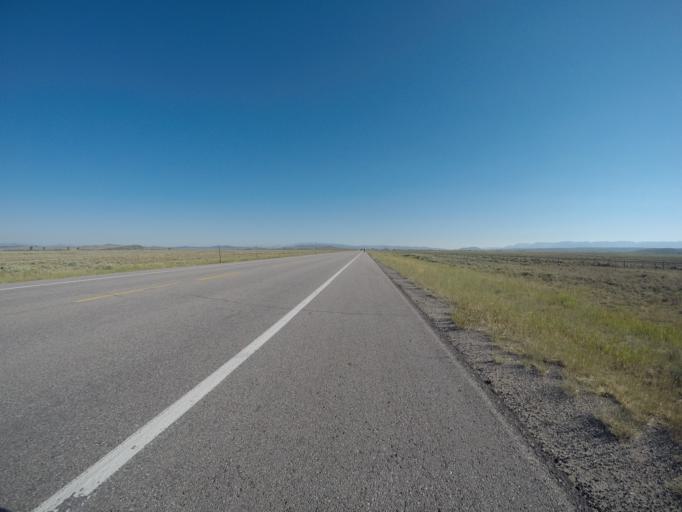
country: US
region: Wyoming
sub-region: Sublette County
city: Pinedale
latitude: 42.9564
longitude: -110.0871
